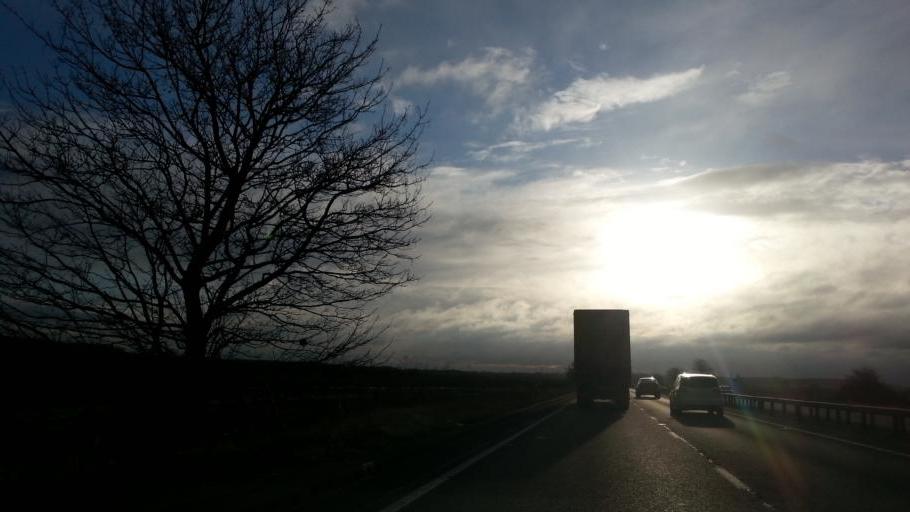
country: GB
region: England
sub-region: Cambridgeshire
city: Great Stukeley
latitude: 52.3559
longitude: -0.2304
